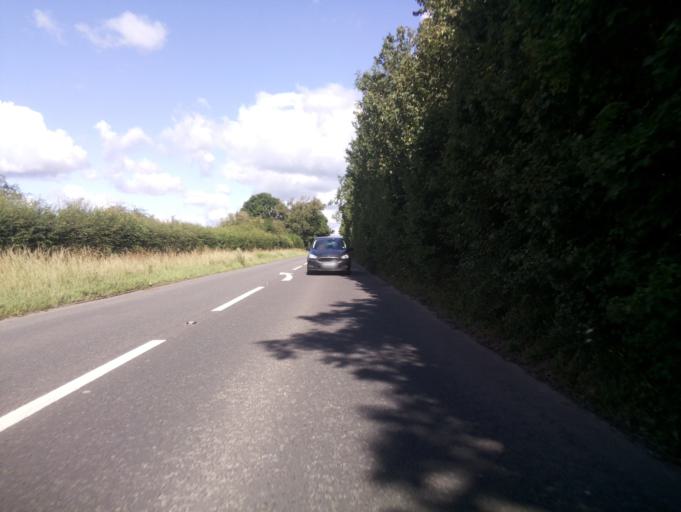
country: GB
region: England
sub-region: Gloucestershire
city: Newent
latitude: 51.9211
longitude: -2.3677
